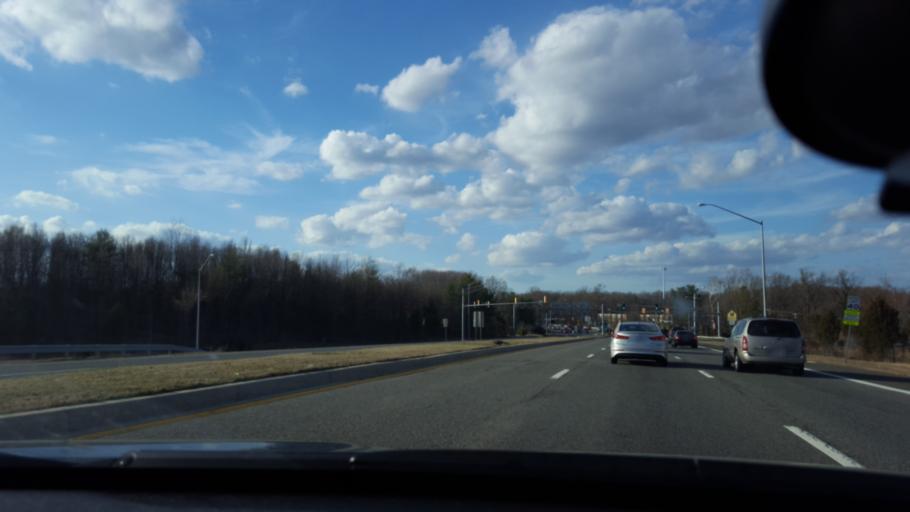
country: US
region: Maryland
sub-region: Prince George's County
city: Bowie
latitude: 38.9537
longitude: -76.7434
